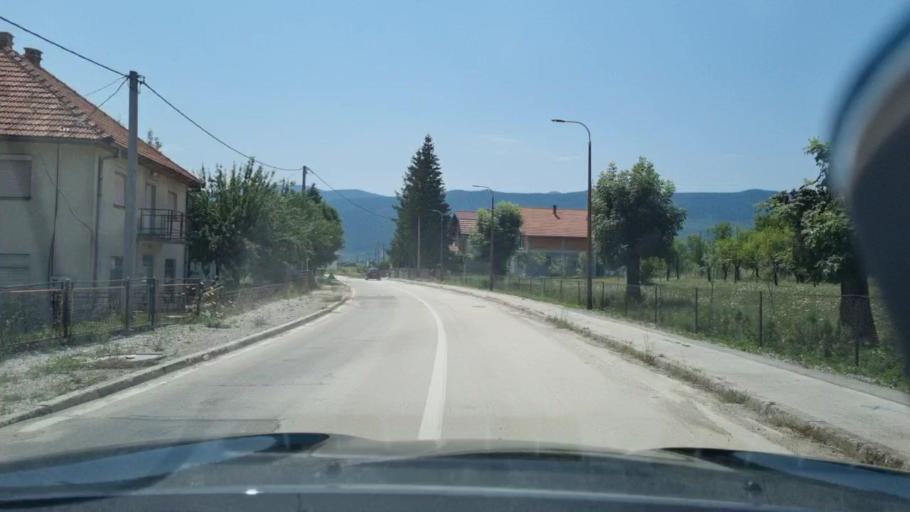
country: BA
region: Federation of Bosnia and Herzegovina
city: Sanica
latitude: 44.5442
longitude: 16.3633
